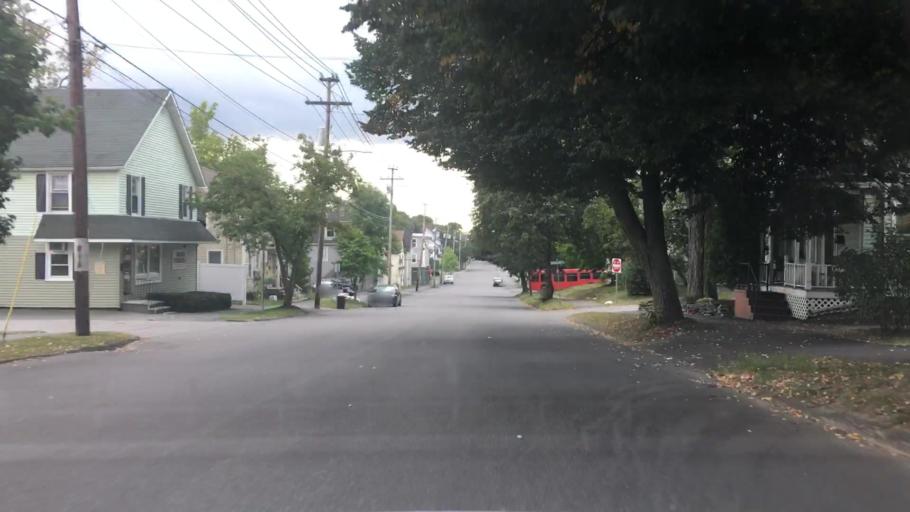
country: US
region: Maine
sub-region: Penobscot County
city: Bangor
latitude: 44.8109
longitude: -68.7724
